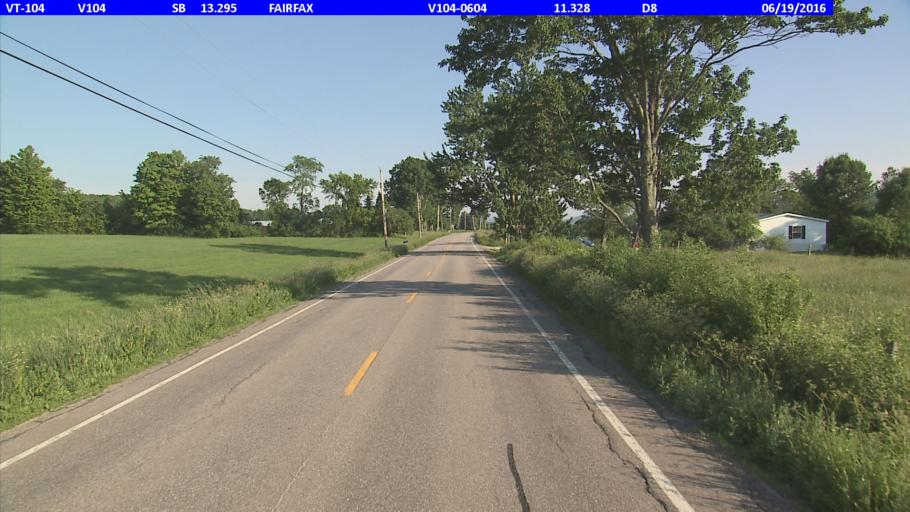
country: US
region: Vermont
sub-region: Franklin County
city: Saint Albans
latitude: 44.7471
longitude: -73.0523
